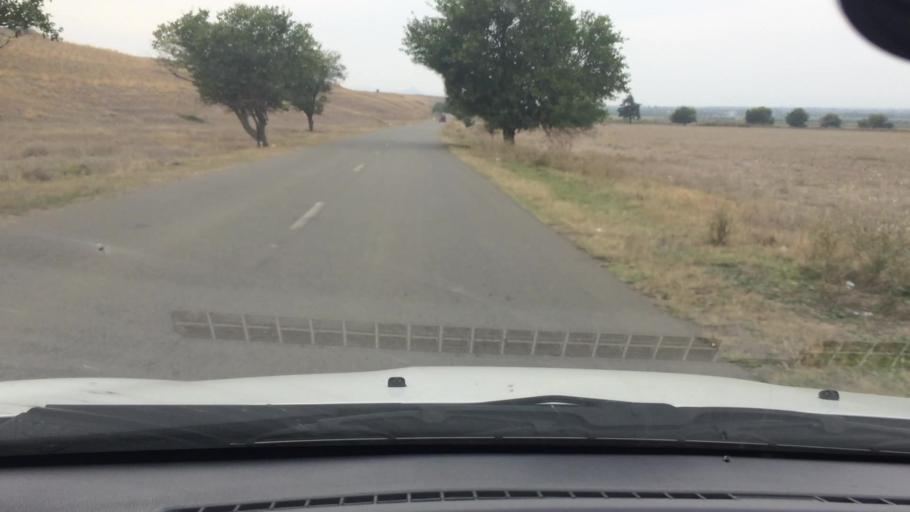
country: AM
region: Tavush
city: Berdavan
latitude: 41.3376
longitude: 45.0094
